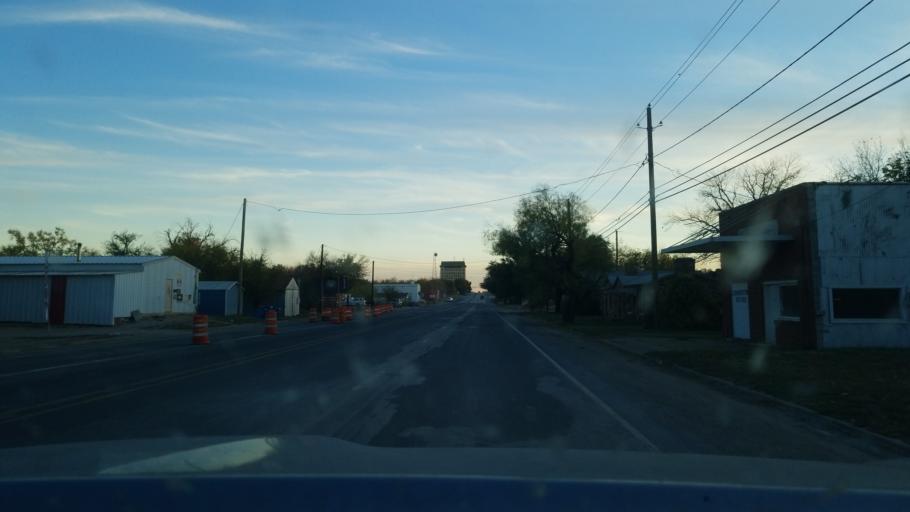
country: US
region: Texas
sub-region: Stephens County
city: Breckenridge
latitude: 32.7631
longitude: -98.9027
